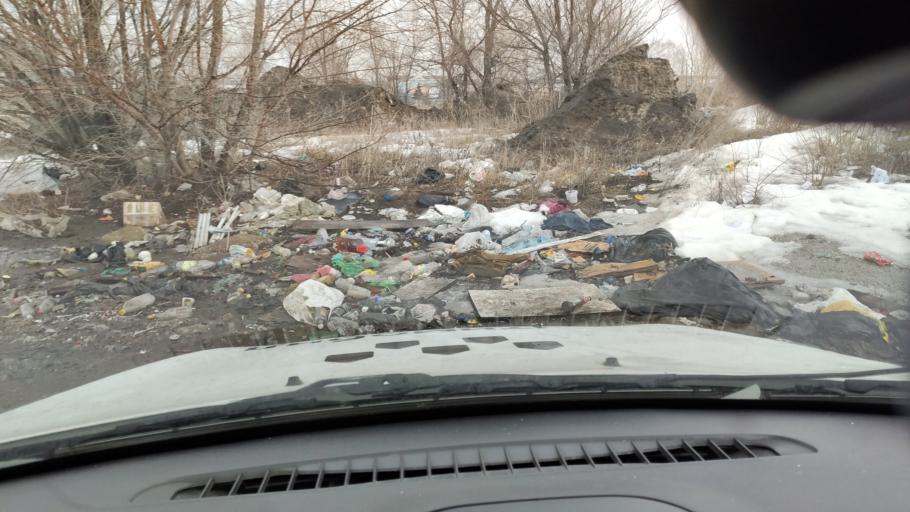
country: RU
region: Samara
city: Tol'yatti
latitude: 53.5562
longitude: 49.2396
